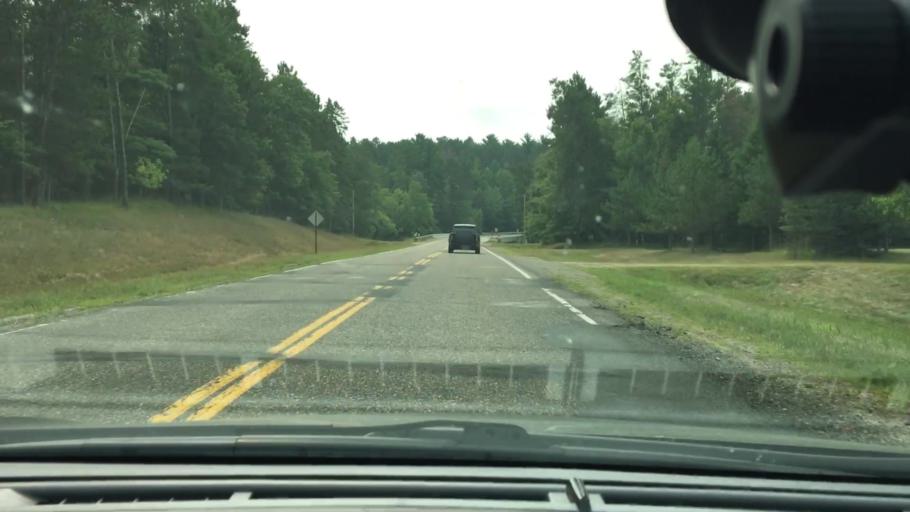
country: US
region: Minnesota
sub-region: Crow Wing County
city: Cross Lake
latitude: 46.6550
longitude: -94.0992
